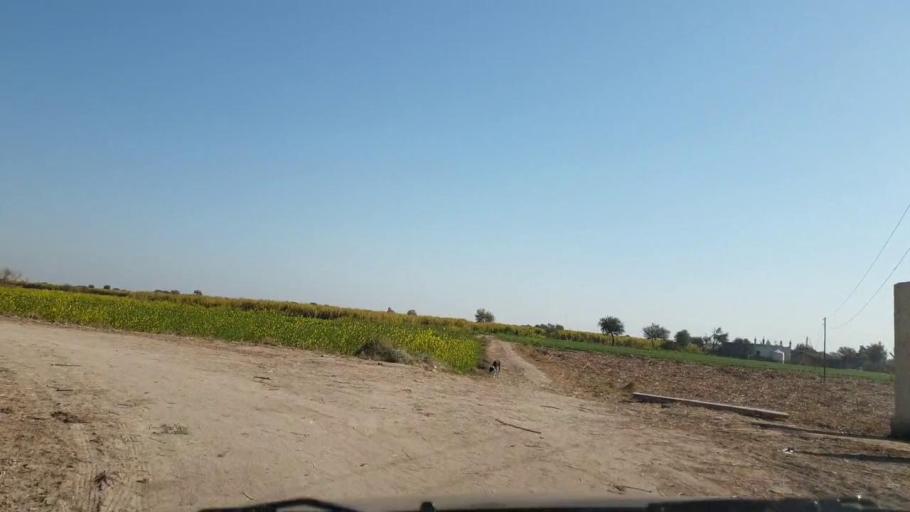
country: PK
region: Sindh
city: Sinjhoro
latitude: 26.1099
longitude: 68.8436
